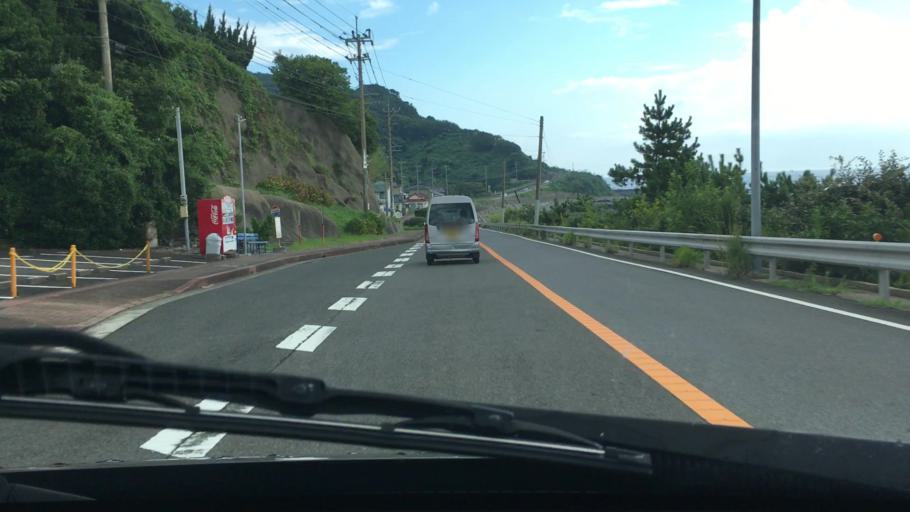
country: JP
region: Nagasaki
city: Togitsu
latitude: 32.8776
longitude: 129.6800
